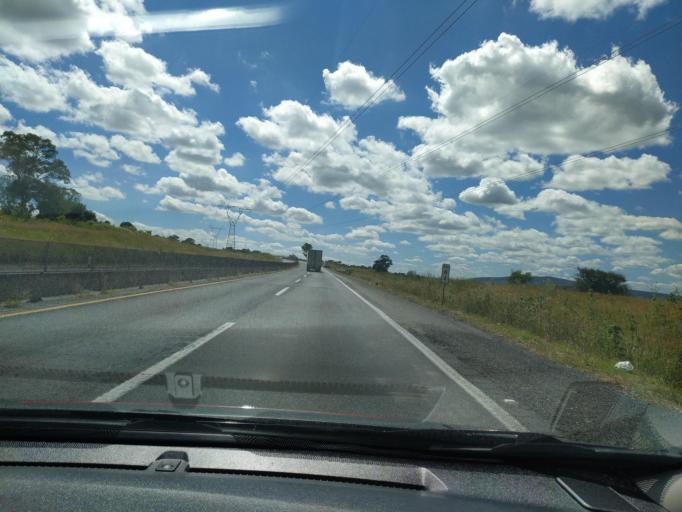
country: MX
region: Jalisco
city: Valle de Guadalupe
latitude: 20.9481
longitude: -102.6465
